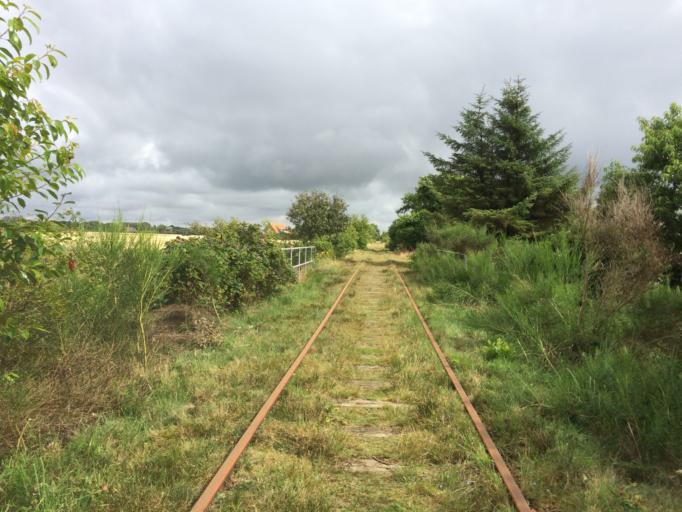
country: DK
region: South Denmark
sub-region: Varde Kommune
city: Oksbol
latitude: 55.7837
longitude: 8.2617
